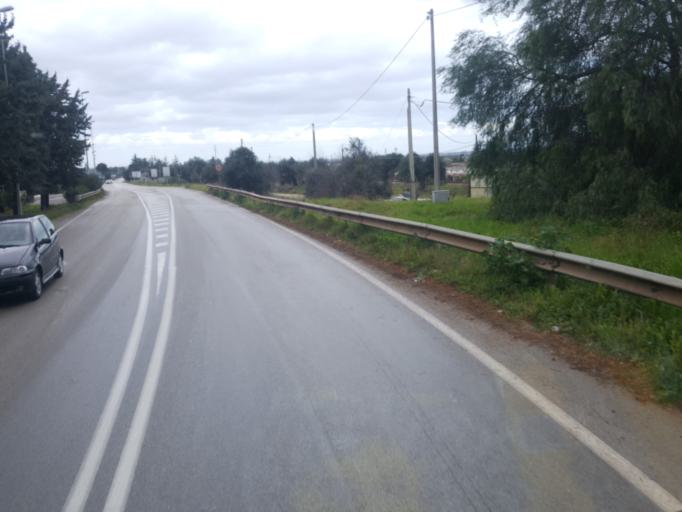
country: IT
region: Apulia
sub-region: Provincia di Bari
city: Conversano
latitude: 40.9787
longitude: 17.0992
